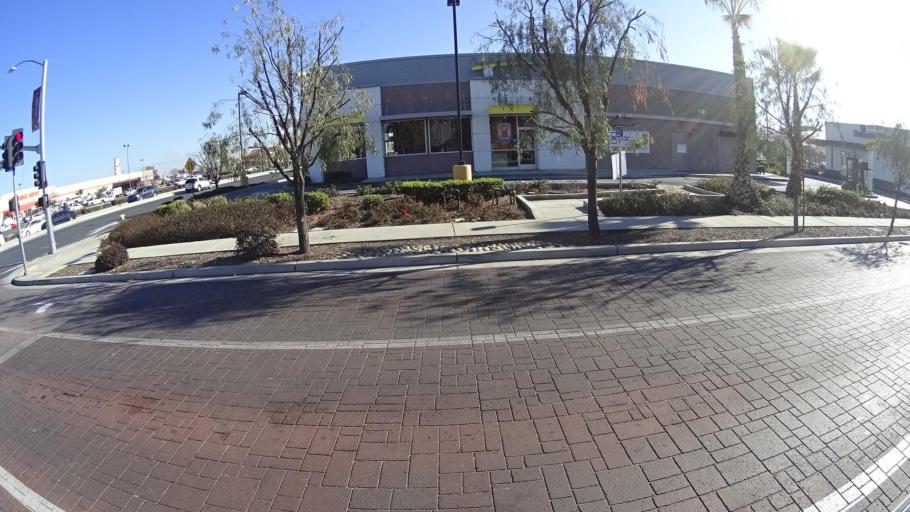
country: US
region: California
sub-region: Kern County
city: Delano
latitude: 35.7466
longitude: -119.2472
